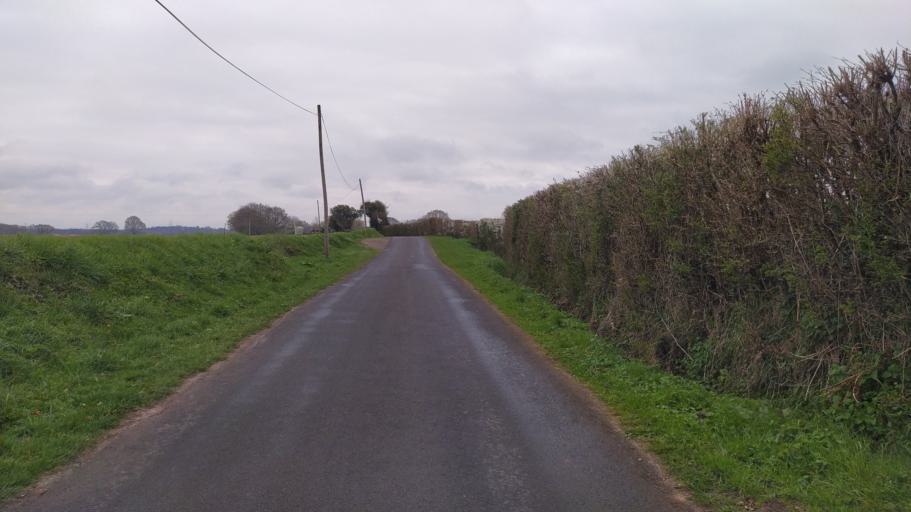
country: GB
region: England
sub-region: West Sussex
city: Petworth
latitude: 51.0269
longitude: -0.5872
